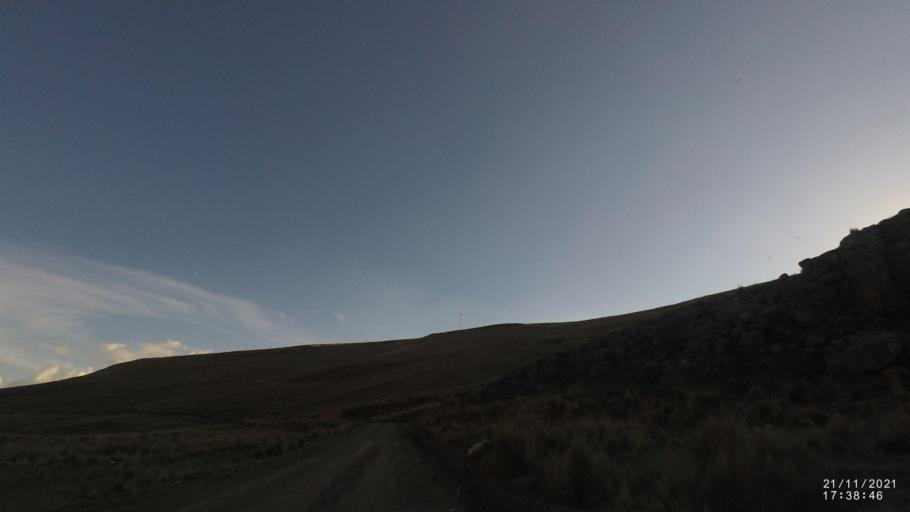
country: BO
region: Cochabamba
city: Cochabamba
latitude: -17.1991
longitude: -66.2468
